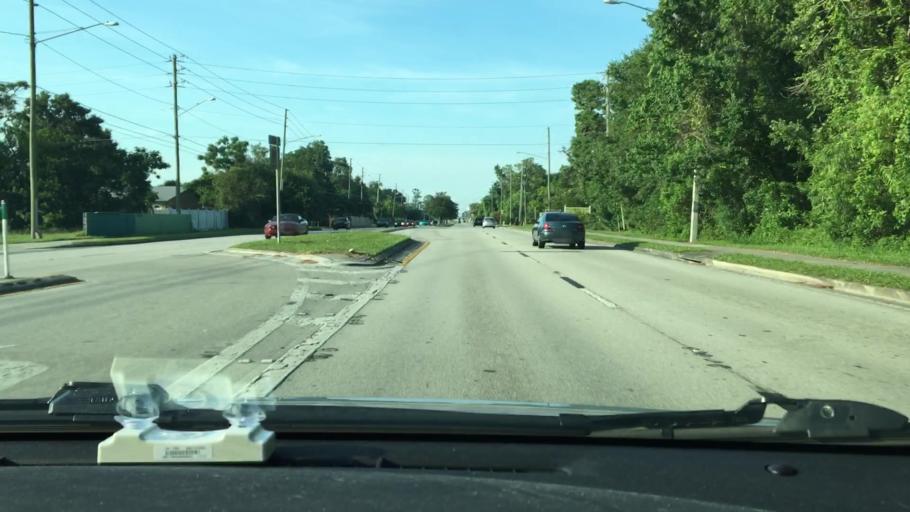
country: US
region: Florida
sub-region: Orange County
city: Union Park
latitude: 28.5798
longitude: -81.2863
